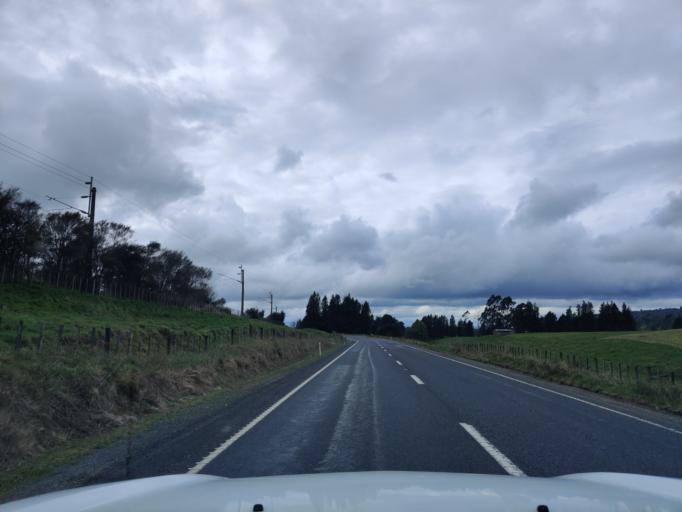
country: NZ
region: Waikato
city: Turangi
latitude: -39.0299
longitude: 175.3820
